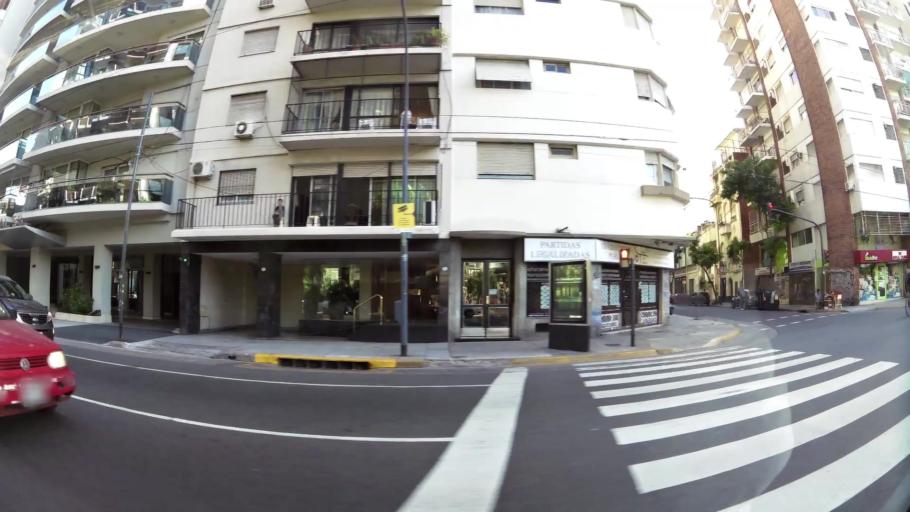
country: AR
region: Buenos Aires F.D.
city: Retiro
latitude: -34.5980
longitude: -58.4065
